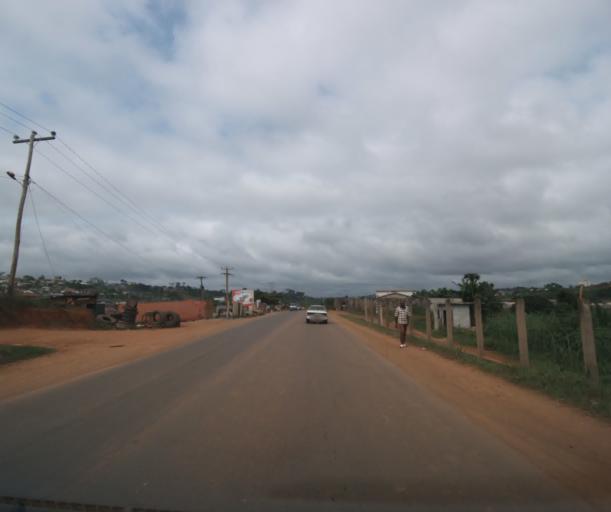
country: CM
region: Centre
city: Yaounde
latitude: 3.8044
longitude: 11.5121
